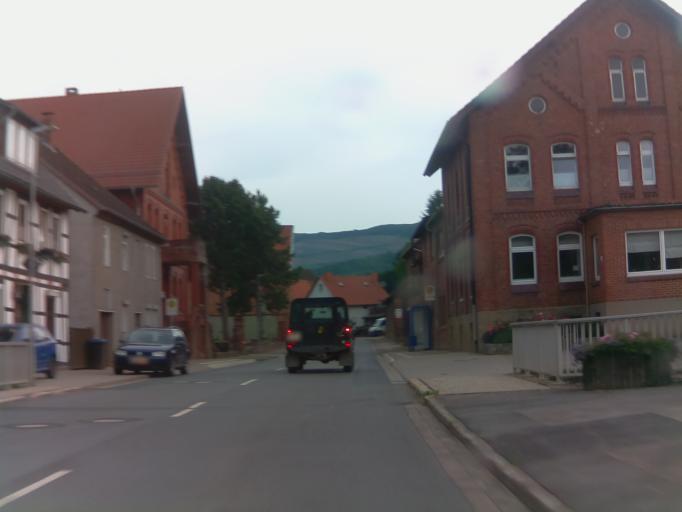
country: DE
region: Lower Saxony
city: Salzhemmendorf
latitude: 52.0449
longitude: 9.5422
